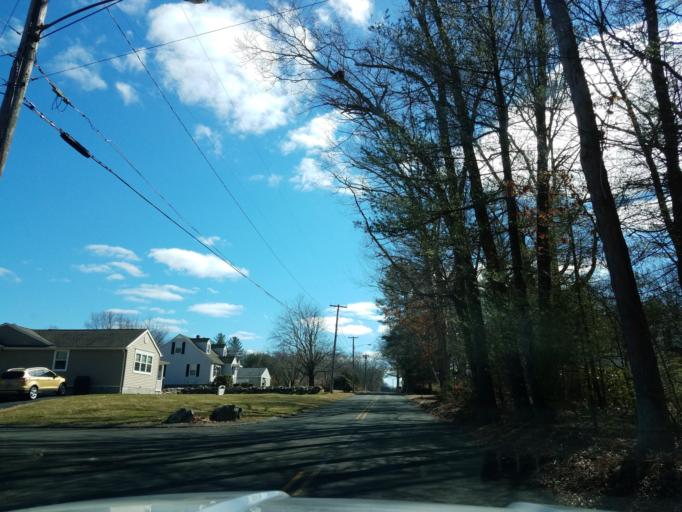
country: US
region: Massachusetts
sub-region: Worcester County
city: Webster
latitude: 42.0238
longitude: -71.8773
